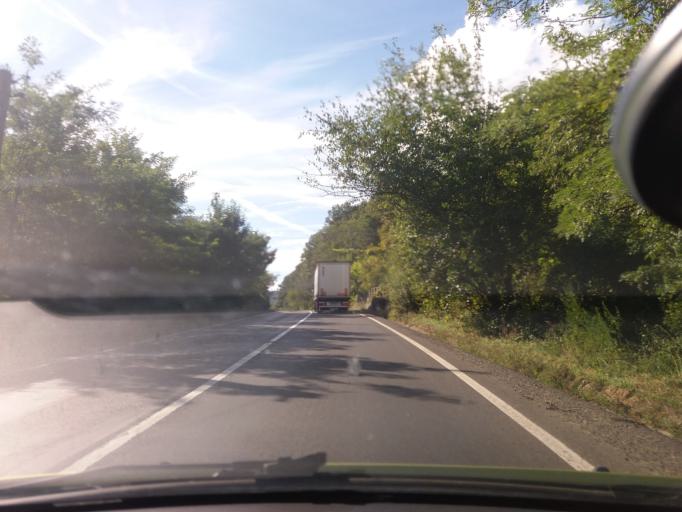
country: RO
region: Hunedoara
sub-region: Comuna Zam
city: Zam
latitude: 46.0122
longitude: 22.4352
